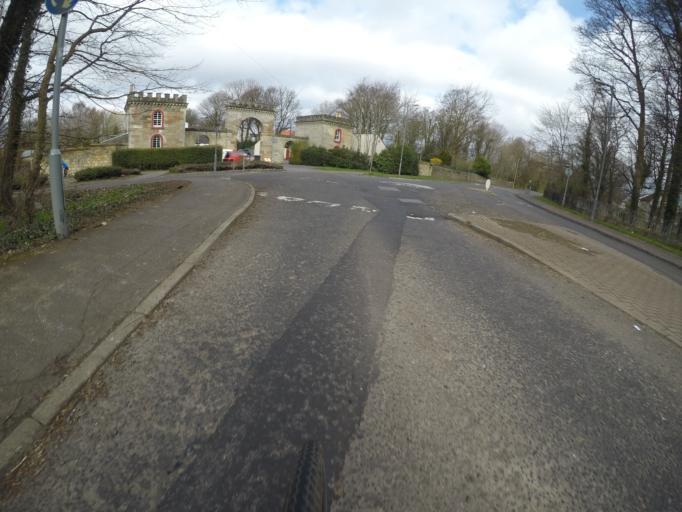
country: GB
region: Scotland
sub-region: North Ayrshire
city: Irvine
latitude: 55.6248
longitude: -4.6422
